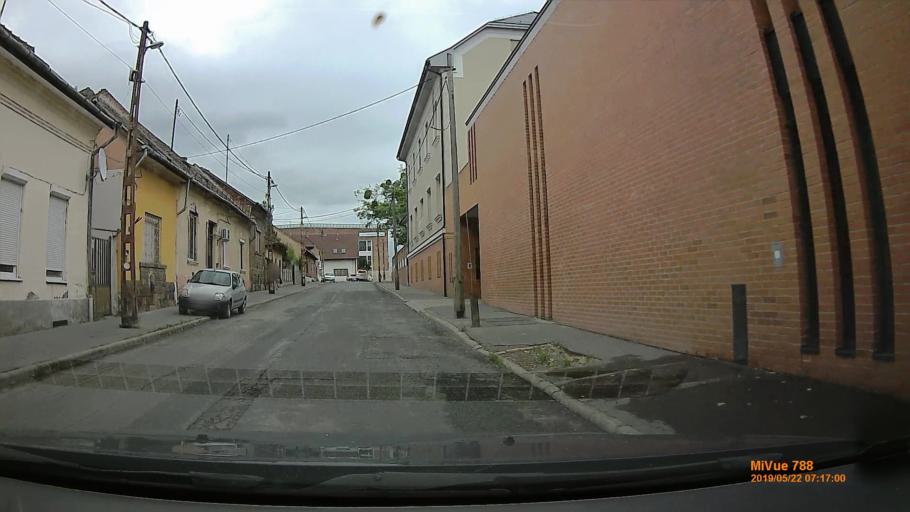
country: HU
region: Budapest
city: Budapest IV. keruelet
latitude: 47.5756
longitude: 19.0896
